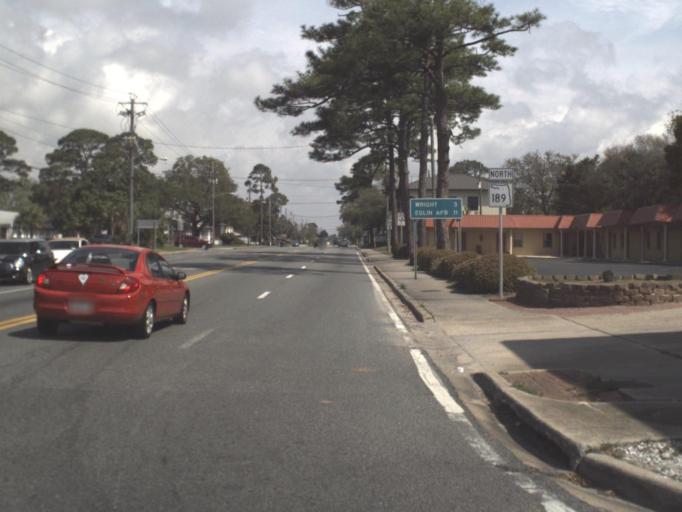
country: US
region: Florida
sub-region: Okaloosa County
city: Fort Walton Beach
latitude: 30.4042
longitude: -86.6131
